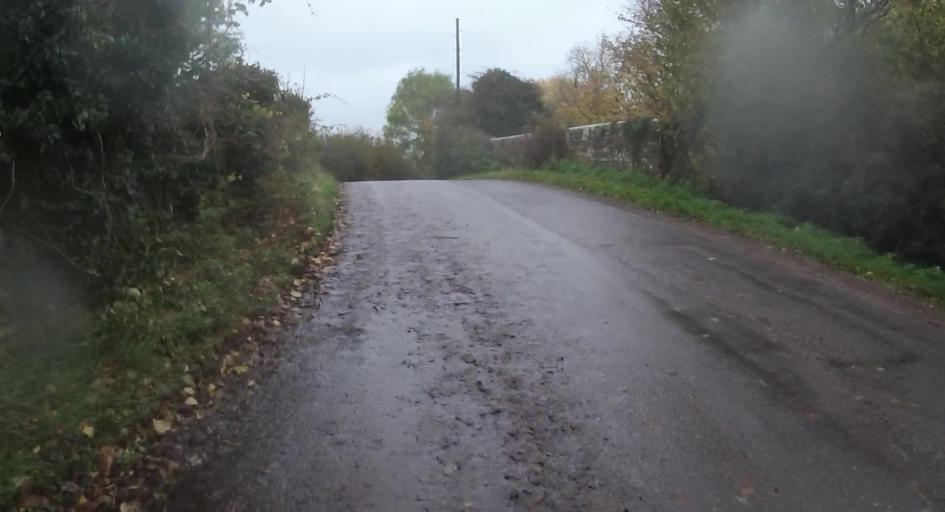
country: GB
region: England
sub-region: Hampshire
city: Kingsley
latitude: 51.1749
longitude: -0.8956
